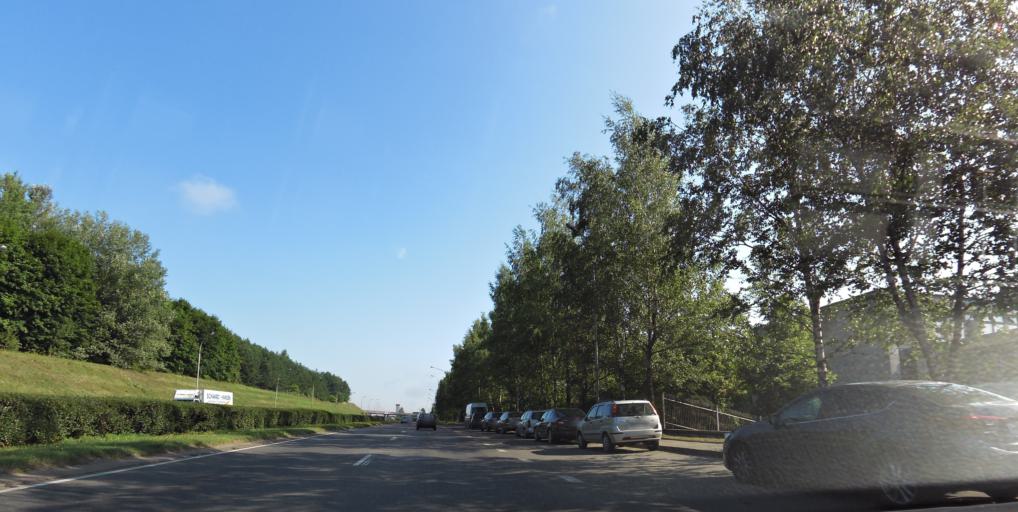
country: LT
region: Vilnius County
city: Seskine
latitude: 54.7073
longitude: 25.2678
